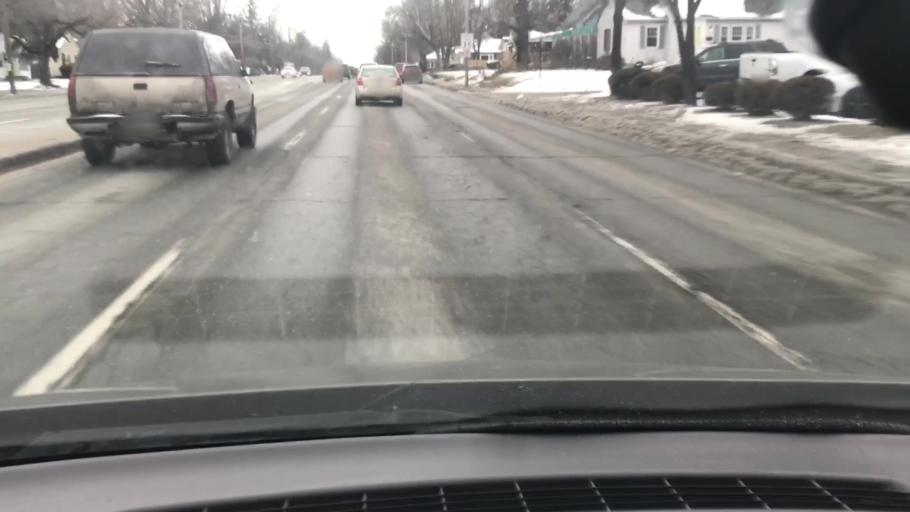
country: US
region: Indiana
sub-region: Marion County
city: Broad Ripple
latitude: 39.8556
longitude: -86.1220
